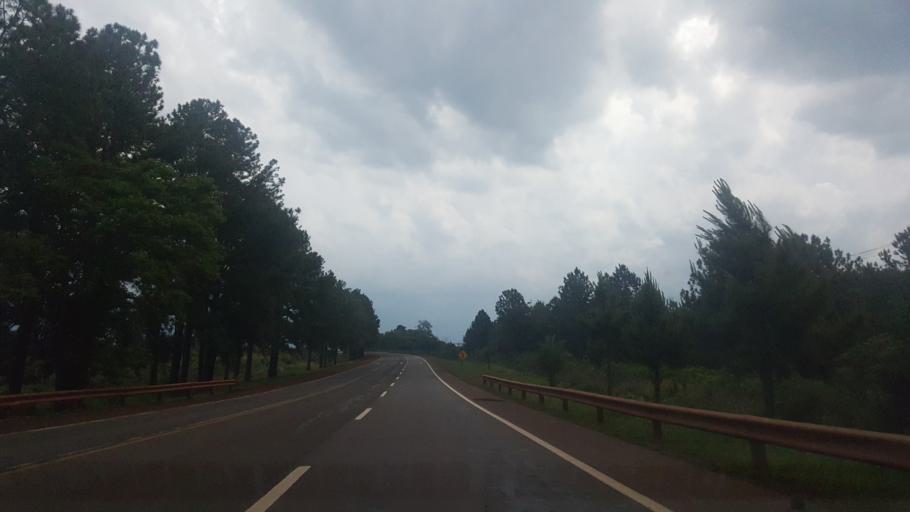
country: AR
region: Misiones
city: Santo Pipo
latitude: -27.1268
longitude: -55.3852
